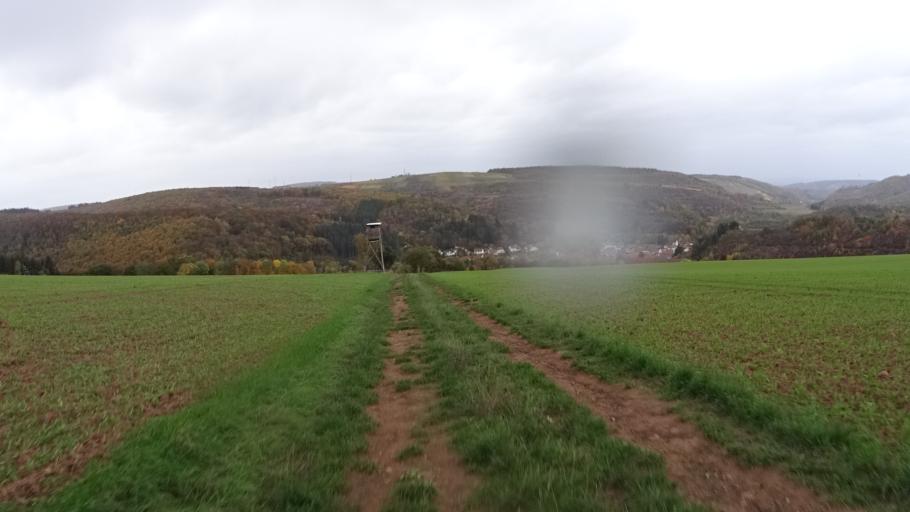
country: DE
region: Rheinland-Pfalz
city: Hochstatten
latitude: 49.7573
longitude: 7.8369
